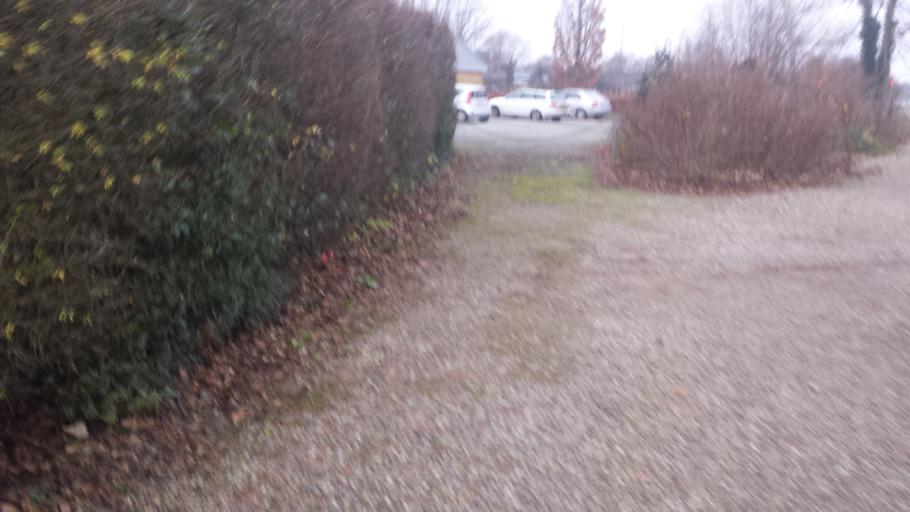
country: DK
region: South Denmark
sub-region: Sonderborg Kommune
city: Grasten
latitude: 54.9080
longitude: 9.5870
